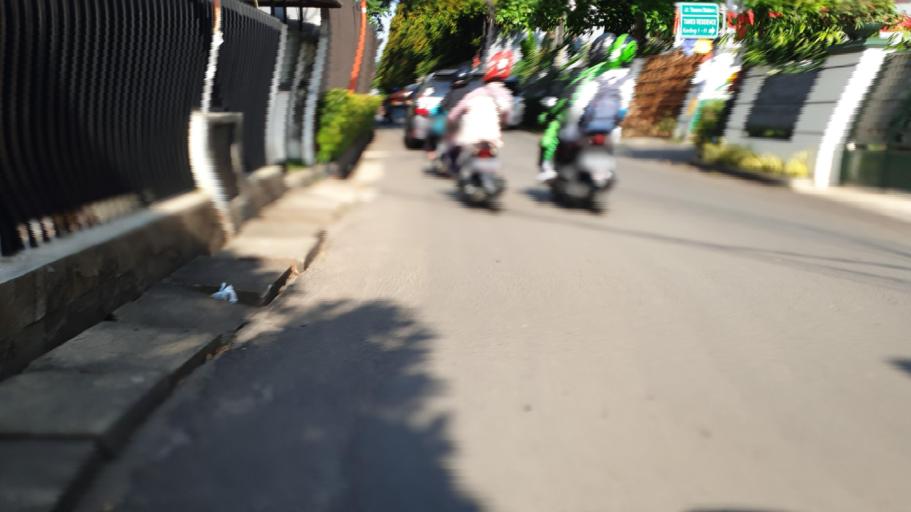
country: ID
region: Jakarta Raya
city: Jakarta
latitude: -6.2939
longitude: 106.8370
